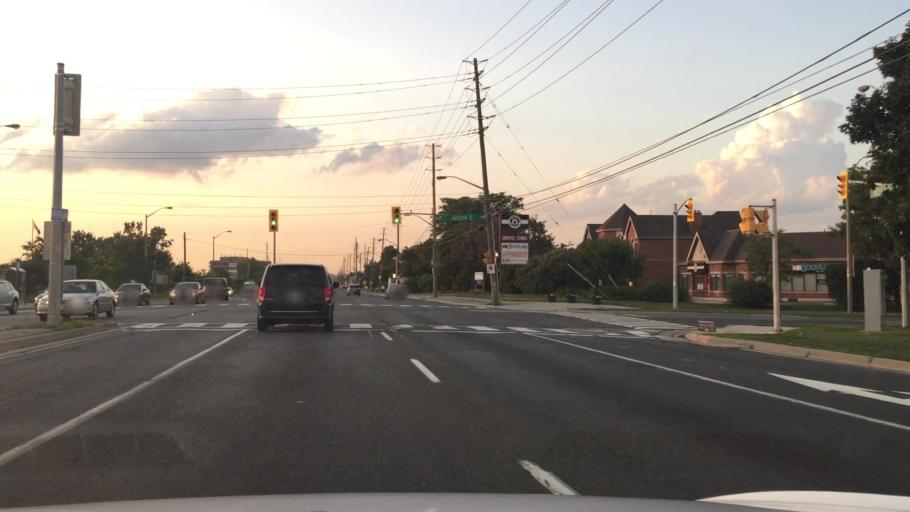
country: CA
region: Ontario
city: Concord
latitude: 43.7956
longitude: -79.4982
